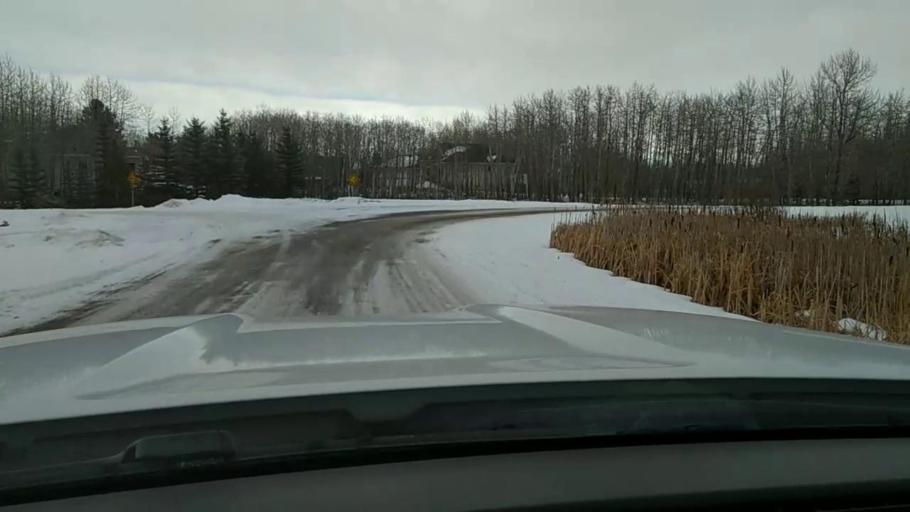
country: CA
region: Alberta
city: Cochrane
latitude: 51.1821
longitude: -114.2565
